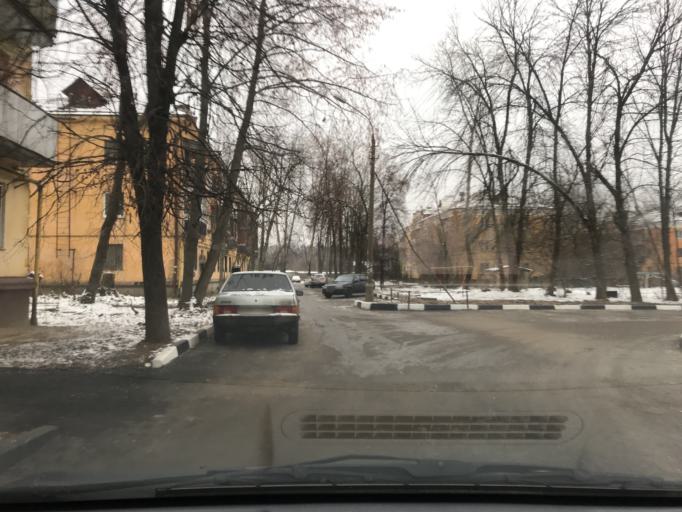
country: RU
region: Moskovskaya
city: Elektrostal'
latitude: 55.8061
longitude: 38.4618
